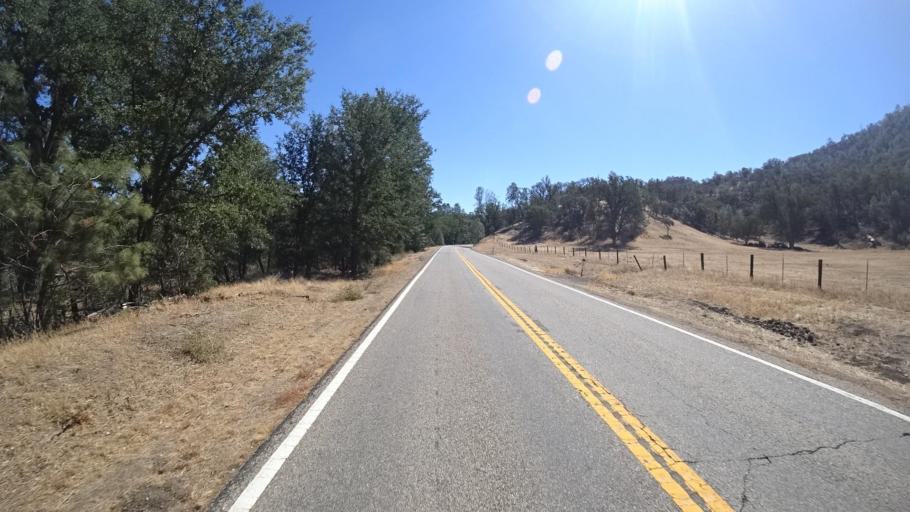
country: US
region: California
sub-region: Fresno County
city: Coalinga
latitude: 36.1992
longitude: -120.7228
